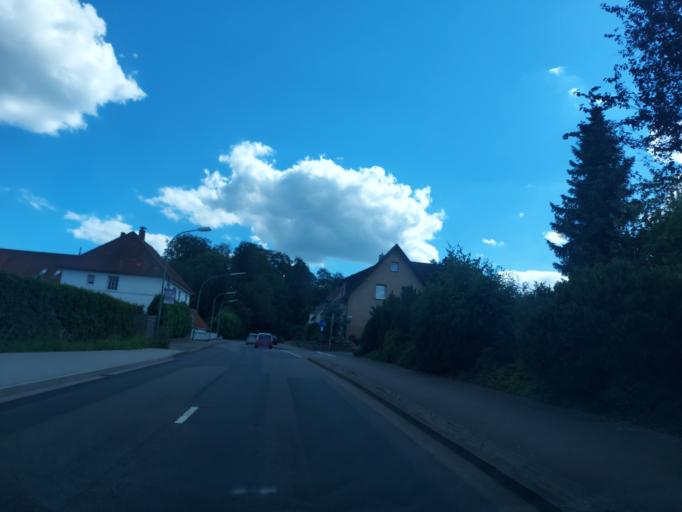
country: DE
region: Lower Saxony
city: Hagen
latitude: 52.2169
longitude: 8.0034
